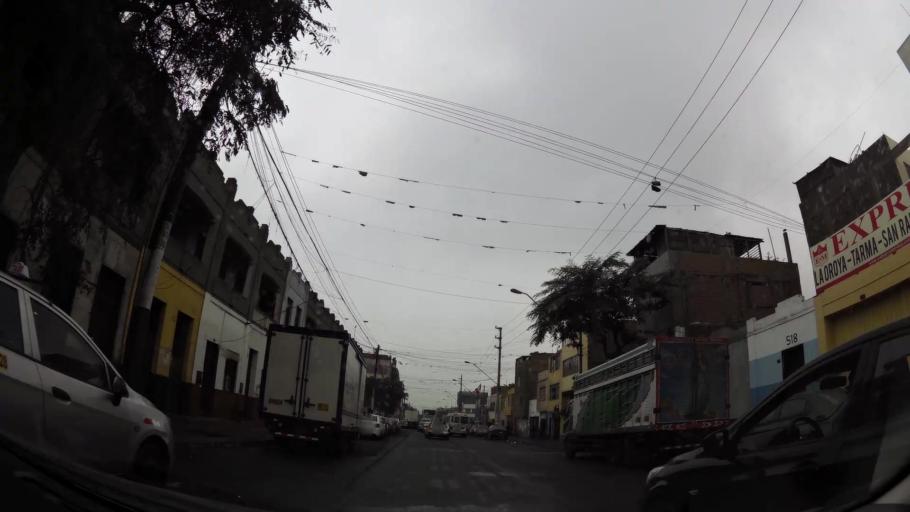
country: PE
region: Lima
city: Lima
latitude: -12.0646
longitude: -77.0276
